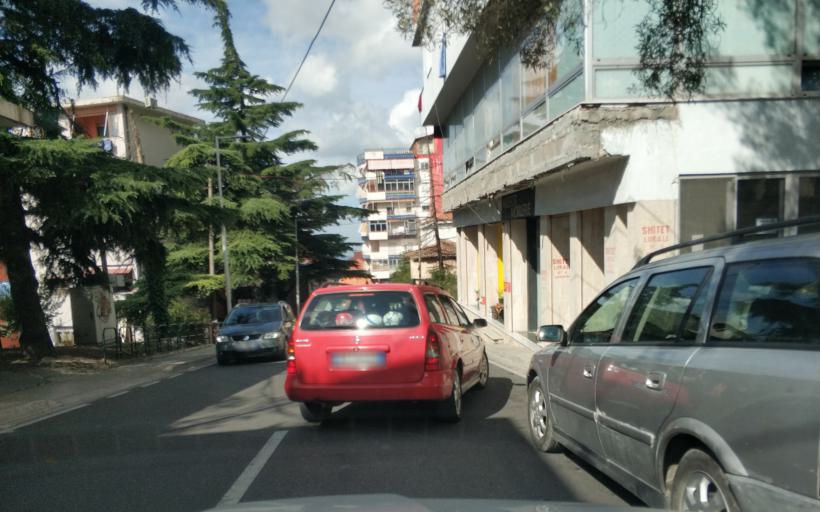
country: AL
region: Durres
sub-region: Rrethi i Krujes
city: Kruje
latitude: 41.5133
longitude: 19.7907
